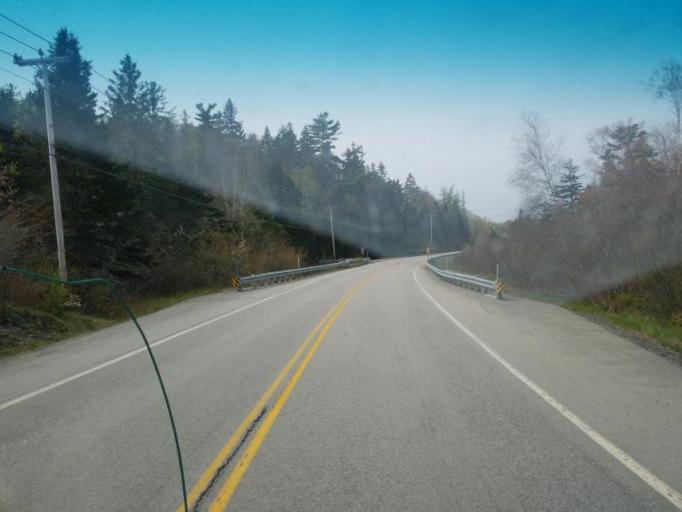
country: US
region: Maine
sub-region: Washington County
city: Eastport
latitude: 44.7970
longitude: -67.1464
